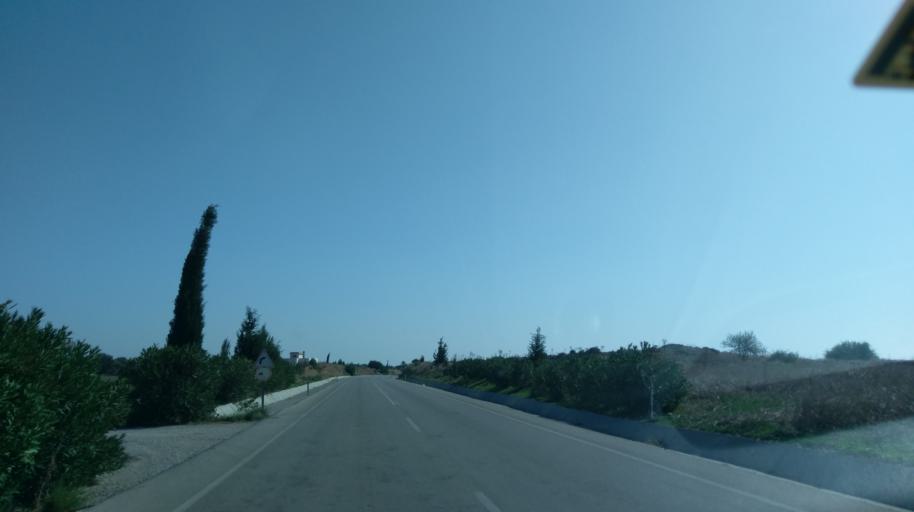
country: CY
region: Ammochostos
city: Leonarisso
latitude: 35.3927
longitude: 34.0071
